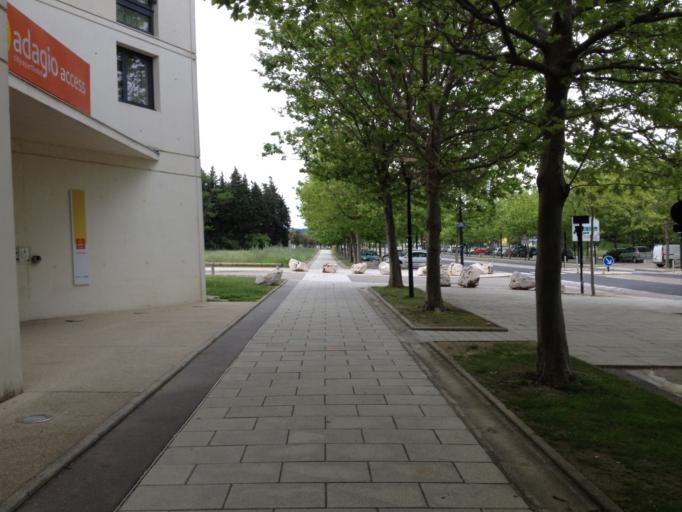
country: FR
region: Provence-Alpes-Cote d'Azur
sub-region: Departement du Vaucluse
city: Avignon
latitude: 43.9263
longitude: 4.7860
